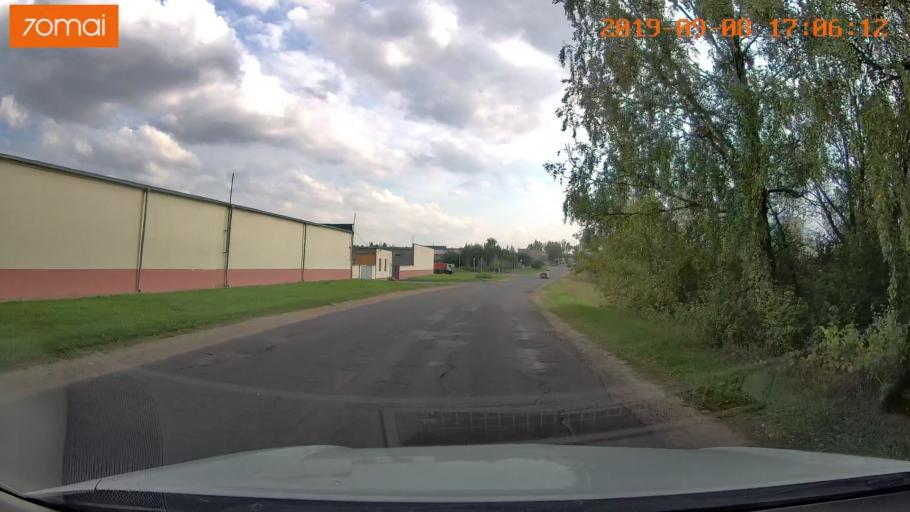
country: BY
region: Grodnenskaya
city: Hrodna
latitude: 53.6725
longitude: 23.9533
